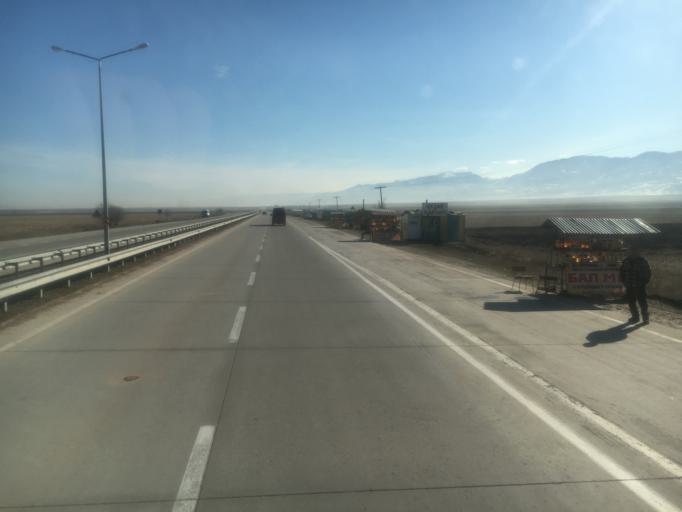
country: KZ
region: Zhambyl
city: Lugovoy
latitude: 42.9056
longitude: 72.9123
